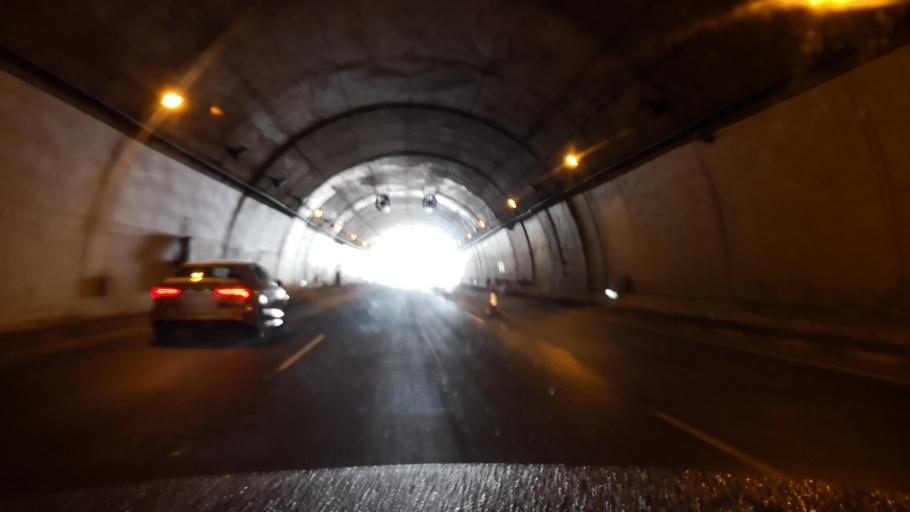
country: ES
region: Castille and Leon
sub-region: Provincia de Zamora
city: Requejo
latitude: 42.0381
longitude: -6.8144
